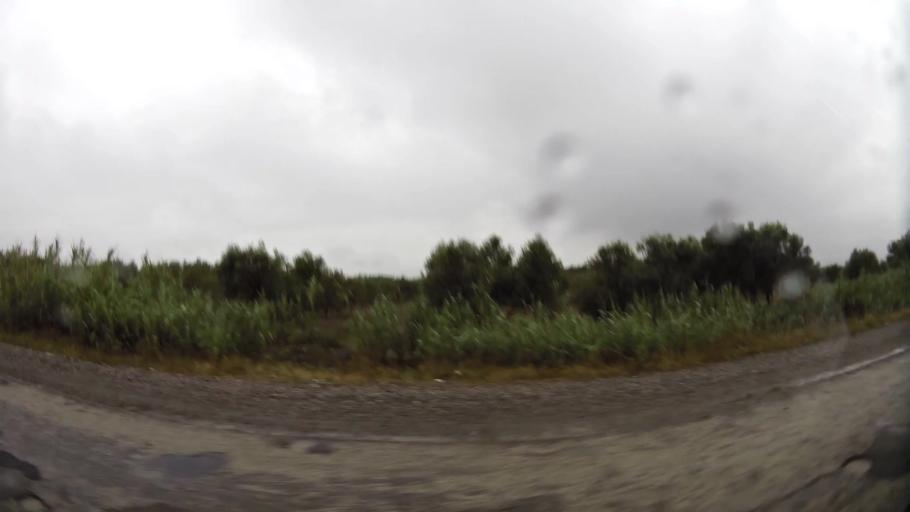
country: MA
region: Taza-Al Hoceima-Taounate
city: Imzourene
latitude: 35.1428
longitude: -3.8076
